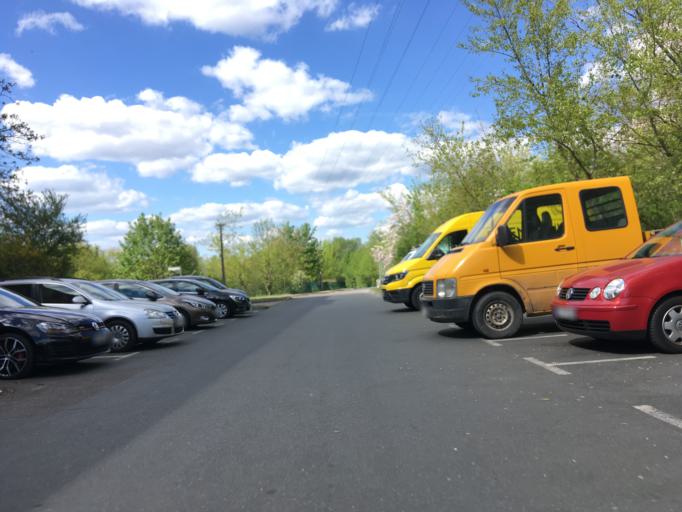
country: DE
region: Berlin
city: Hellersdorf
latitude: 52.5357
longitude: 13.6151
